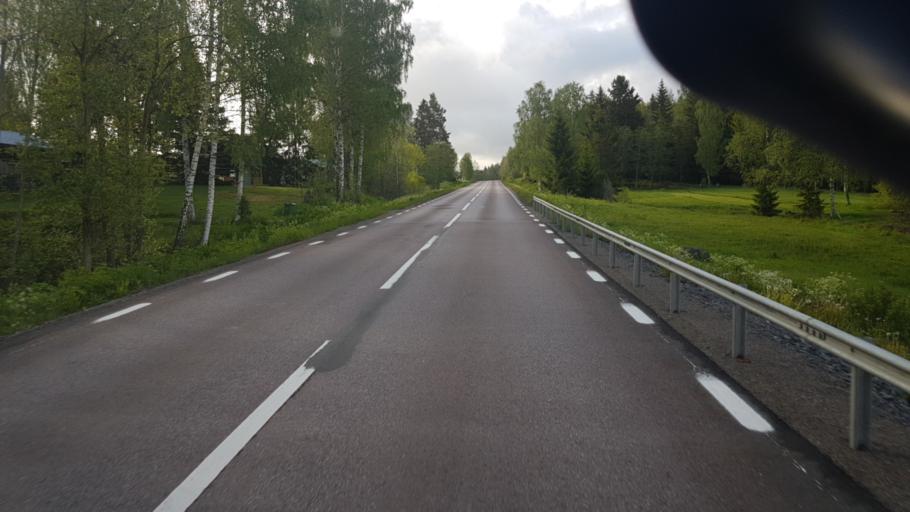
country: SE
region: Vaermland
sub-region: Eda Kommun
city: Amotfors
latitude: 59.7340
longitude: 12.2196
